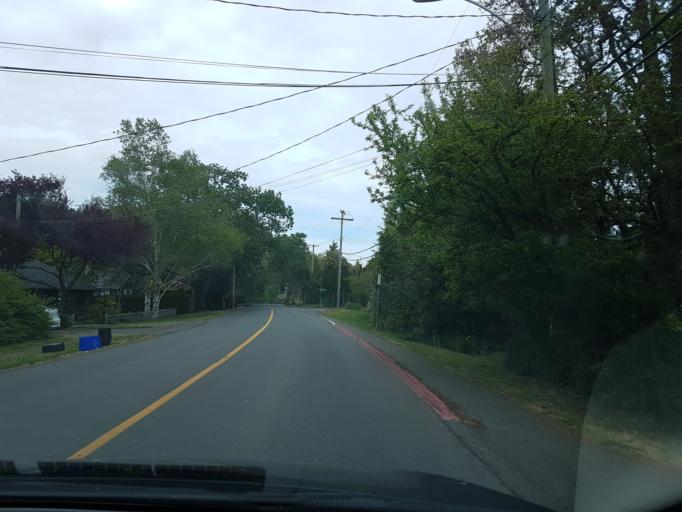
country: CA
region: British Columbia
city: Oak Bay
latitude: 48.4834
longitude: -123.3391
